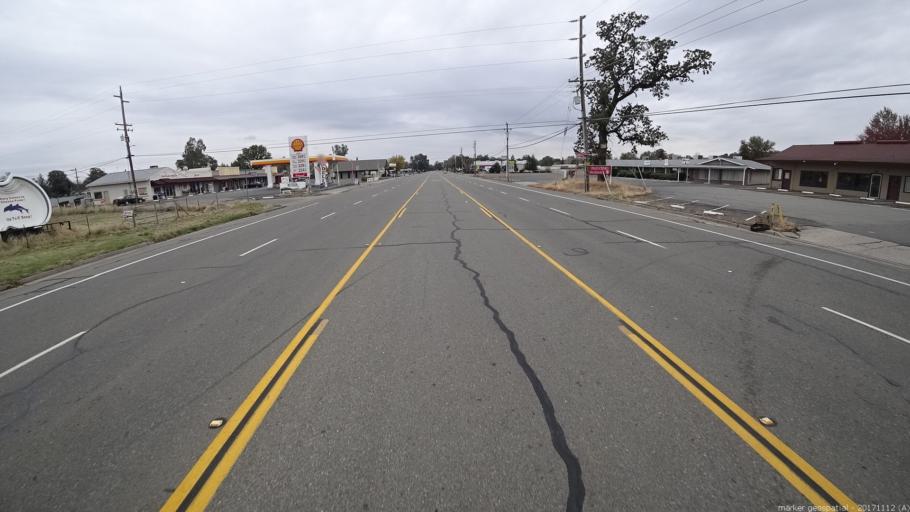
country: US
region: California
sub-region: Shasta County
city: Palo Cedro
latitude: 40.5546
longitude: -122.2383
